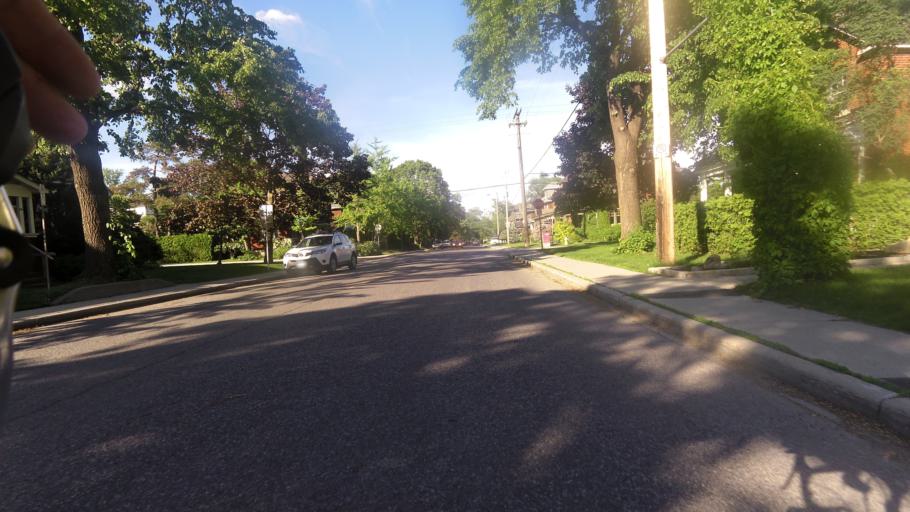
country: CA
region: Ontario
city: Ottawa
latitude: 45.4011
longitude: -75.6951
